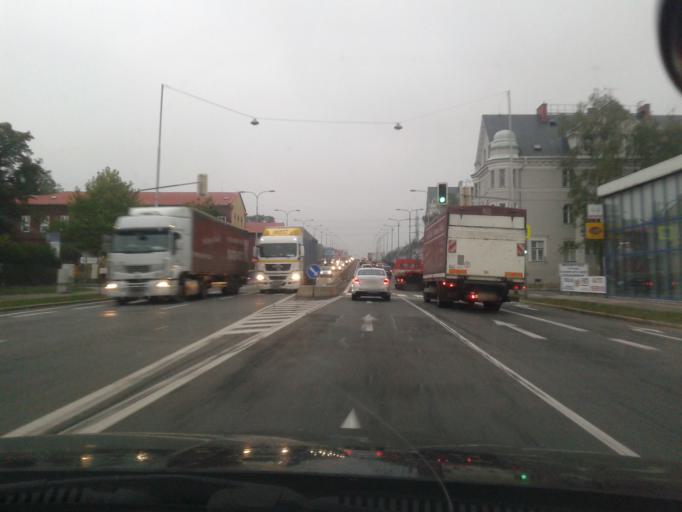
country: CZ
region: Moravskoslezsky
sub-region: Okres Ostrava-Mesto
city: Ostrava
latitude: 49.8055
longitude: 18.2651
